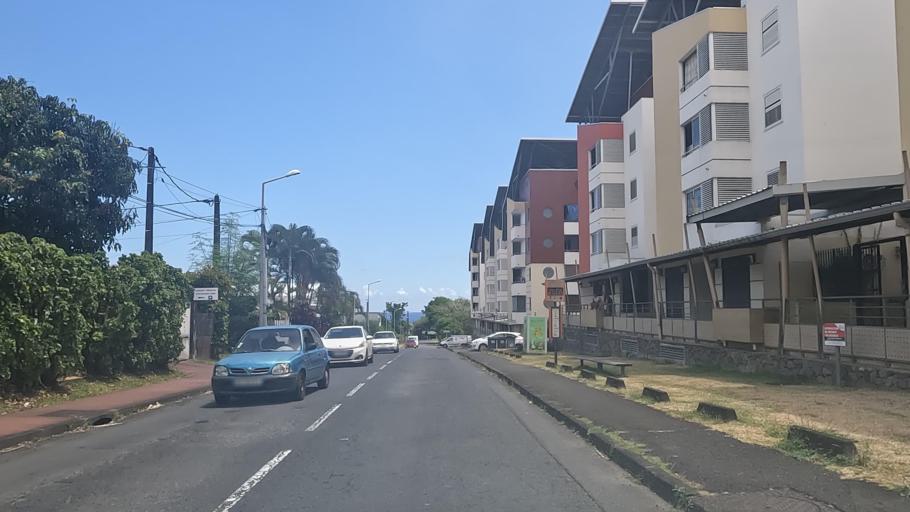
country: RE
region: Reunion
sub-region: Reunion
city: Saint-Benoit
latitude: -21.0323
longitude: 55.7086
